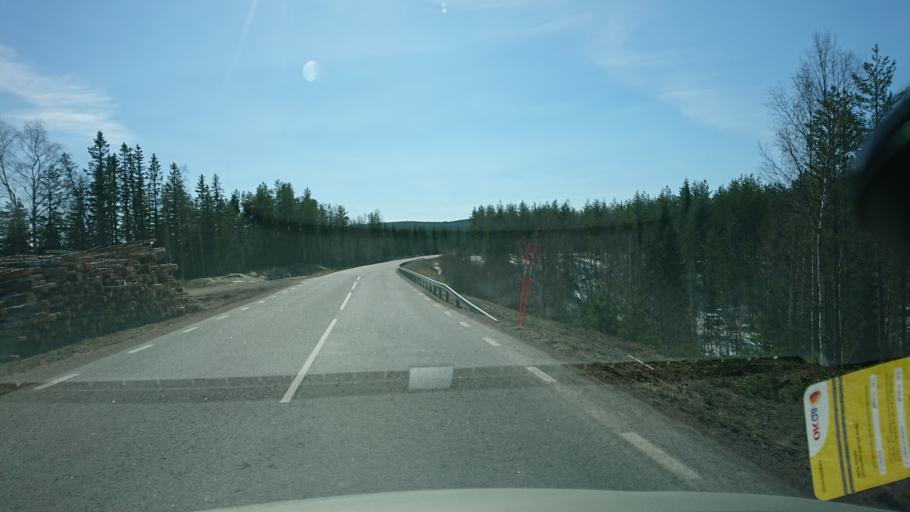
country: SE
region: Vaesternorrland
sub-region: Solleftea Kommun
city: As
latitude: 63.6426
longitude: 16.4567
